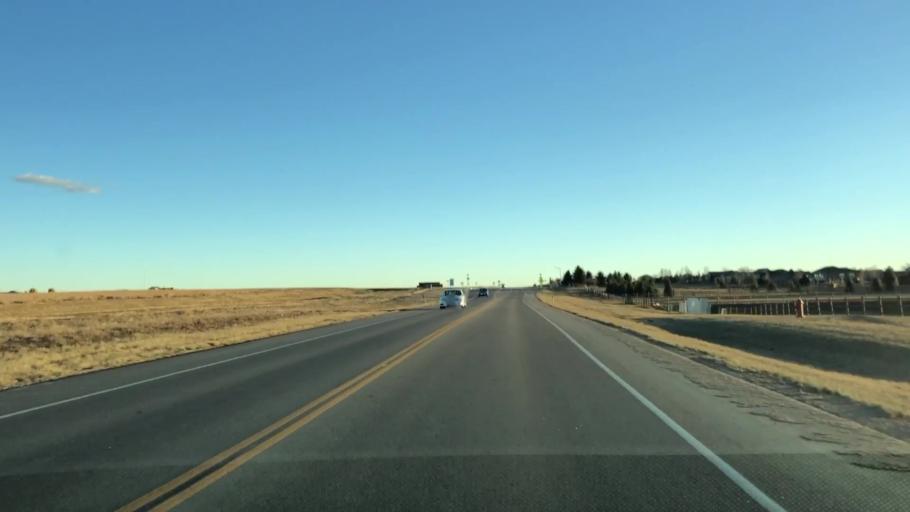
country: US
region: Colorado
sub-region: Weld County
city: Windsor
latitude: 40.4487
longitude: -104.9442
